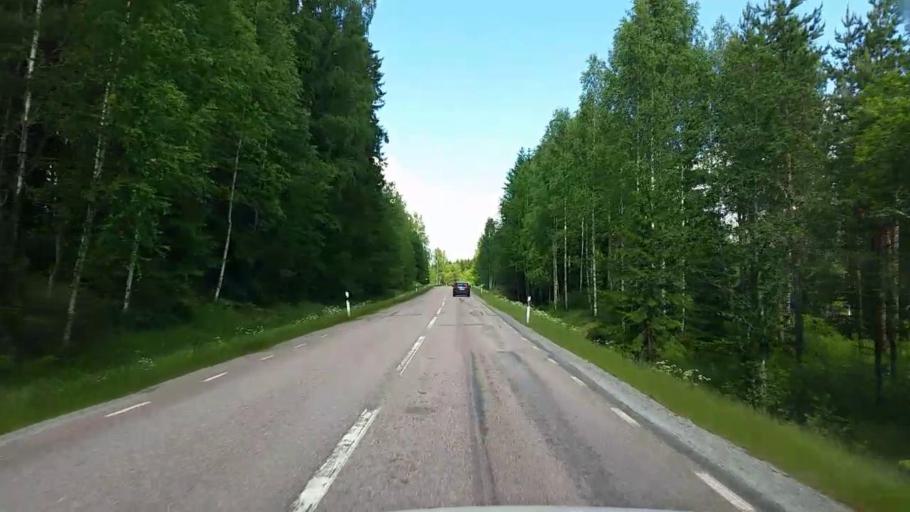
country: SE
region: Vaestmanland
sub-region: Fagersta Kommun
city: Fagersta
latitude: 59.9394
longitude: 15.8090
